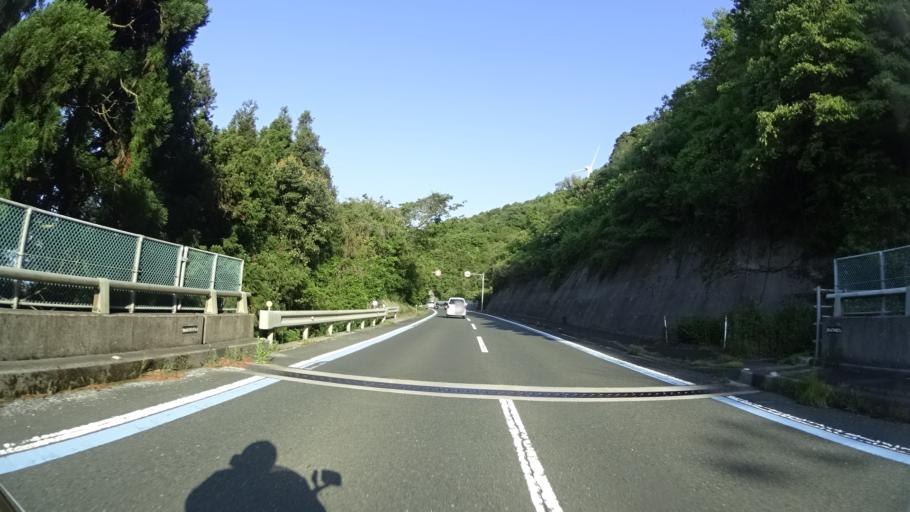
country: JP
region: Ehime
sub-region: Nishiuwa-gun
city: Ikata-cho
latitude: 33.4316
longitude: 132.2231
